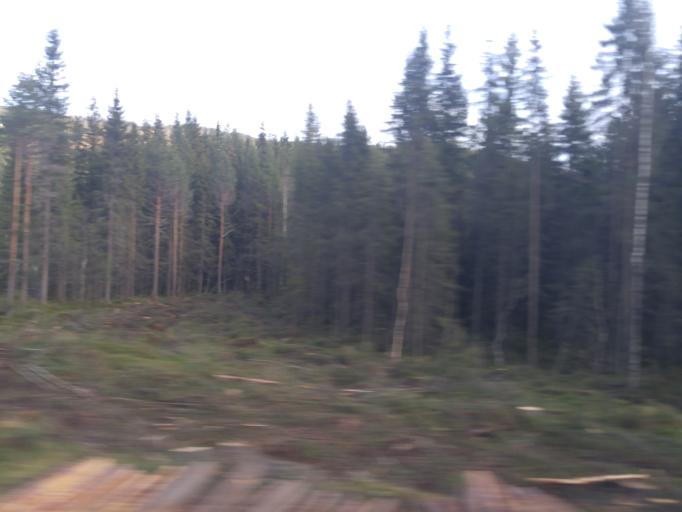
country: NO
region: Oppland
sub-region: Nord-Aurdal
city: Fagernes
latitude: 61.0319
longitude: 9.1756
